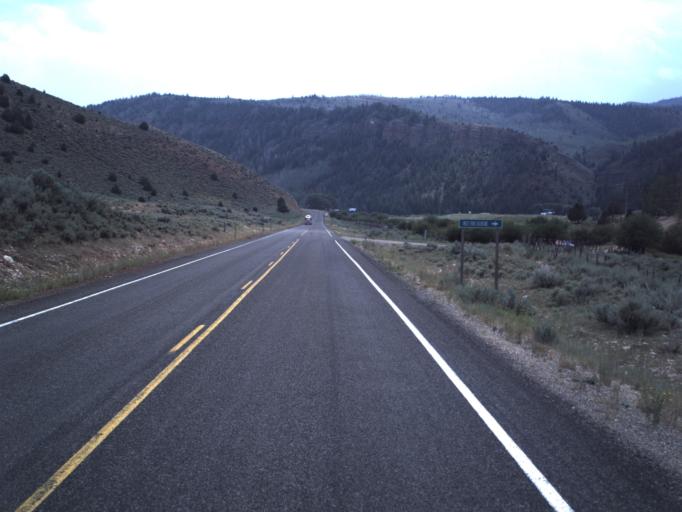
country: US
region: Utah
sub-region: Summit County
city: Francis
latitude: 40.4580
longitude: -110.8909
